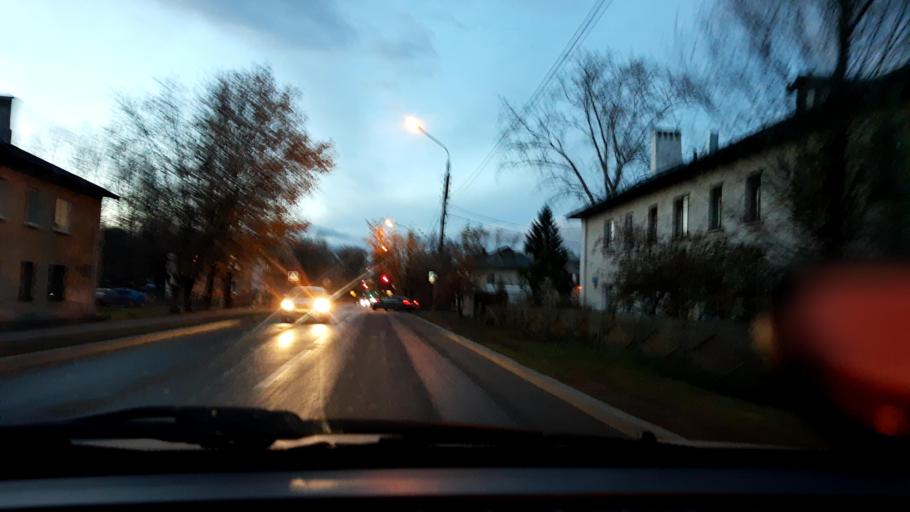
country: RU
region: Nizjnij Novgorod
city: Burevestnik
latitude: 56.2312
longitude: 43.8569
